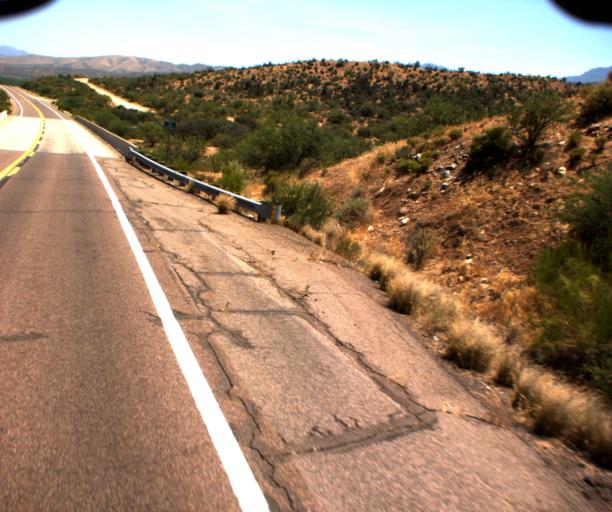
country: US
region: Arizona
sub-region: Gila County
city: Tonto Basin
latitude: 33.7904
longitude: -111.2664
